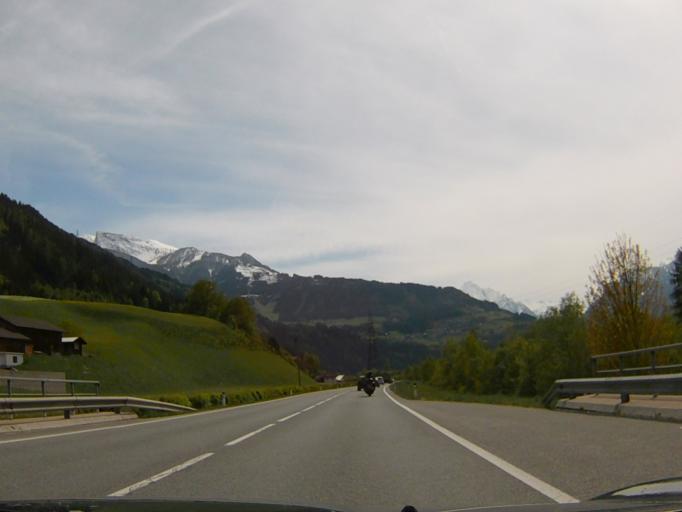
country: AT
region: Tyrol
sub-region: Politischer Bezirk Schwaz
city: Rohrberg
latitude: 47.2520
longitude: 11.9022
